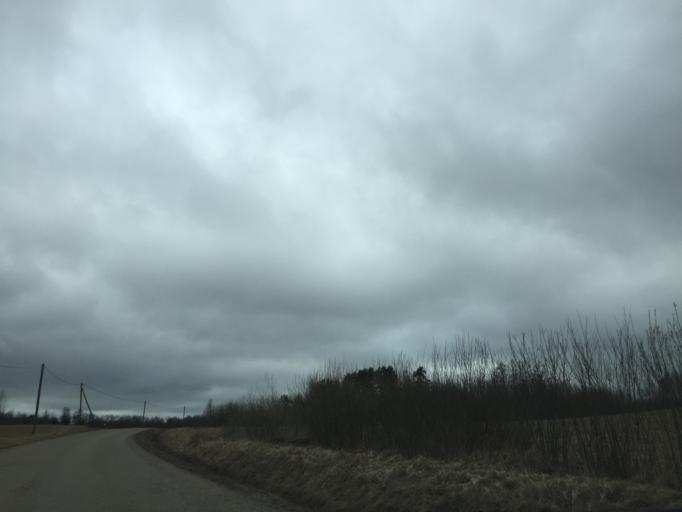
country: LV
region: Ilukste
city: Ilukste
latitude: 56.0337
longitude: 26.2081
